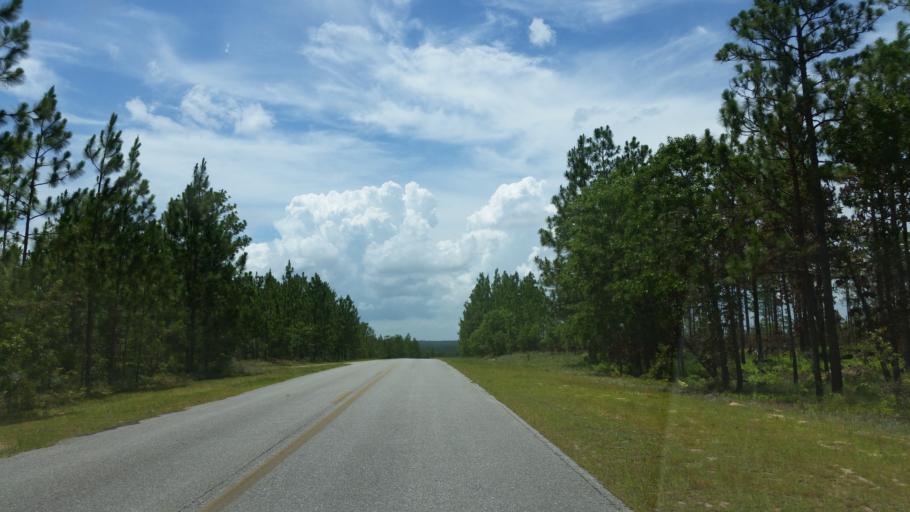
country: US
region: Florida
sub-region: Okaloosa County
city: Crestview
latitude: 30.7164
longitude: -86.7795
